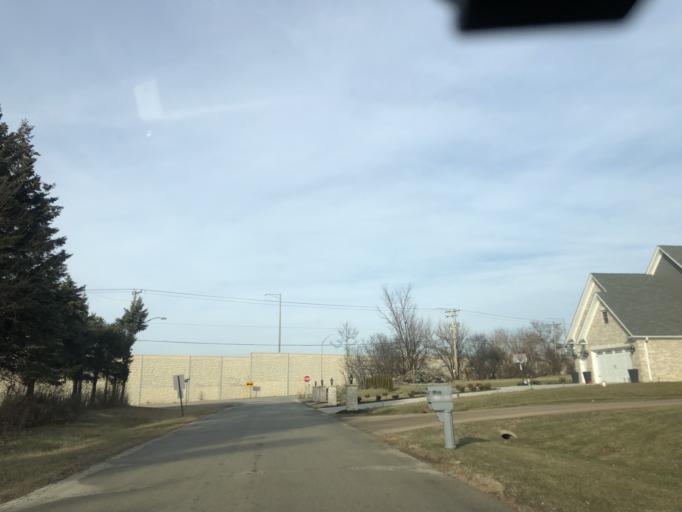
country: US
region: Illinois
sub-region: Cook County
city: Lemont
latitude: 41.7133
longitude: -88.0114
